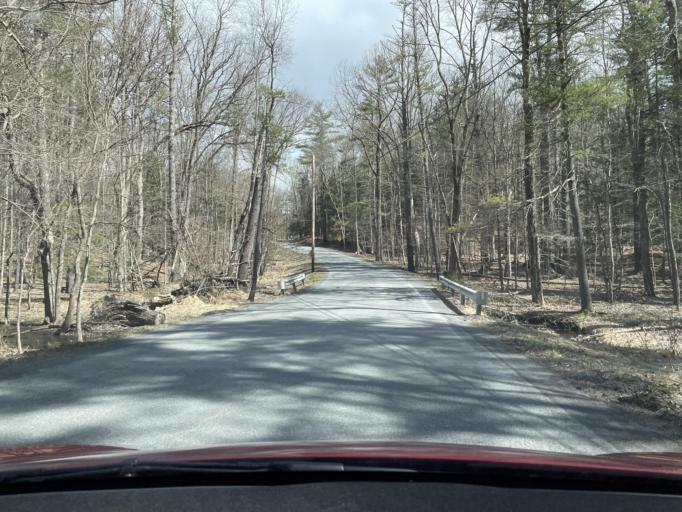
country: US
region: New York
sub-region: Ulster County
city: Zena
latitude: 42.0168
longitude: -74.0685
